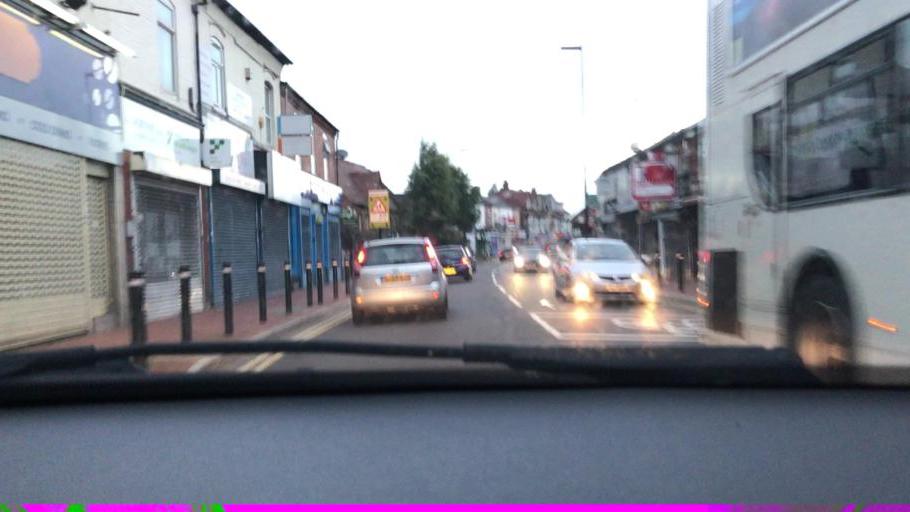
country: GB
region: England
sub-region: Sandwell
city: Smethwick
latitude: 52.4770
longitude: -1.9699
